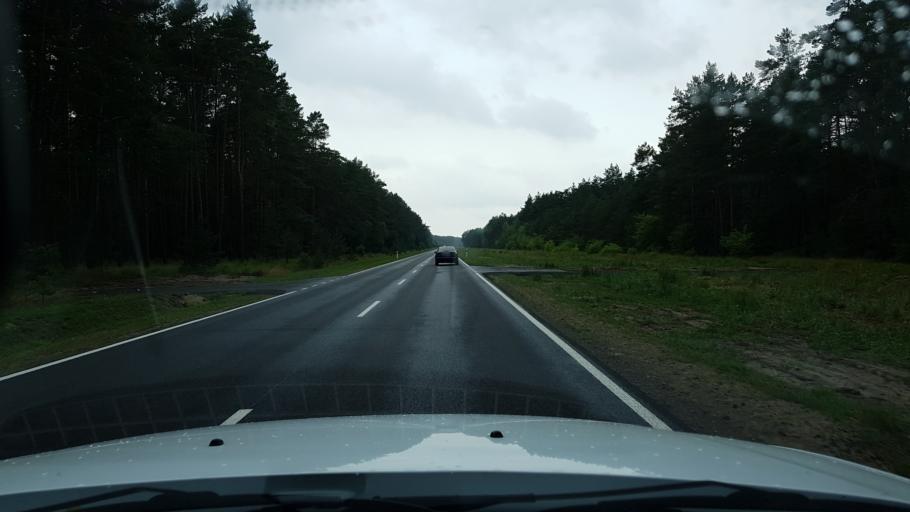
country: PL
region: West Pomeranian Voivodeship
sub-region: Powiat stargardzki
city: Kobylanka
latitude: 53.4319
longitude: 14.8440
